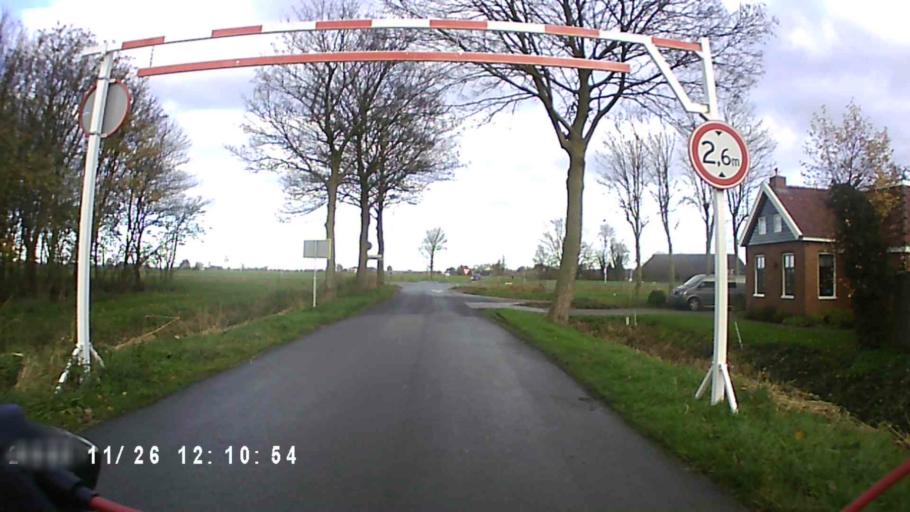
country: NL
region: Groningen
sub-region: Gemeente Bedum
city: Bedum
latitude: 53.3391
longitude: 6.6360
